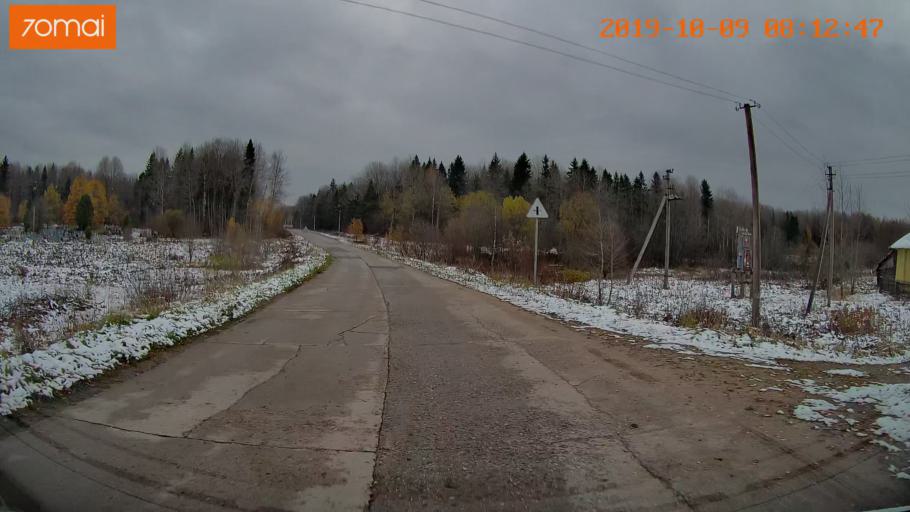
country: RU
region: Vologda
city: Gryazovets
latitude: 58.7207
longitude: 40.1302
